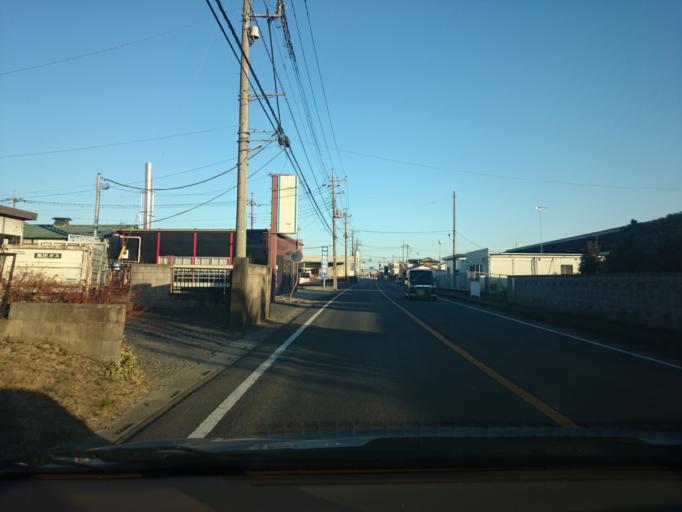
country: JP
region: Saitama
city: Kazo
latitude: 36.1054
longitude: 139.6007
